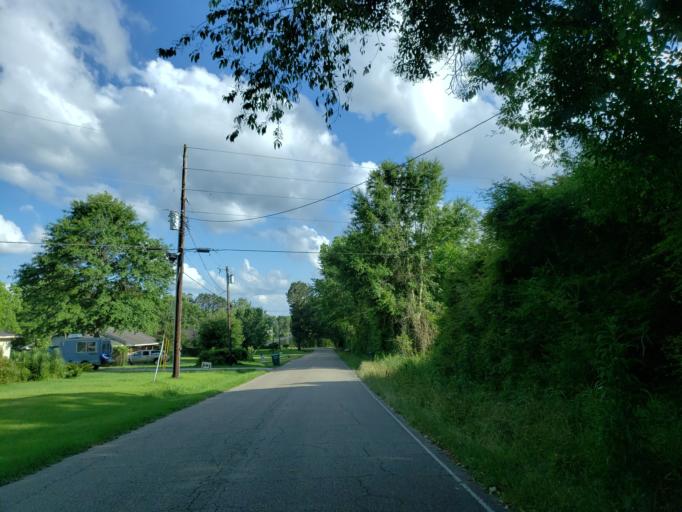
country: US
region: Mississippi
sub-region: Forrest County
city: Petal
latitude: 31.3202
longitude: -89.1971
